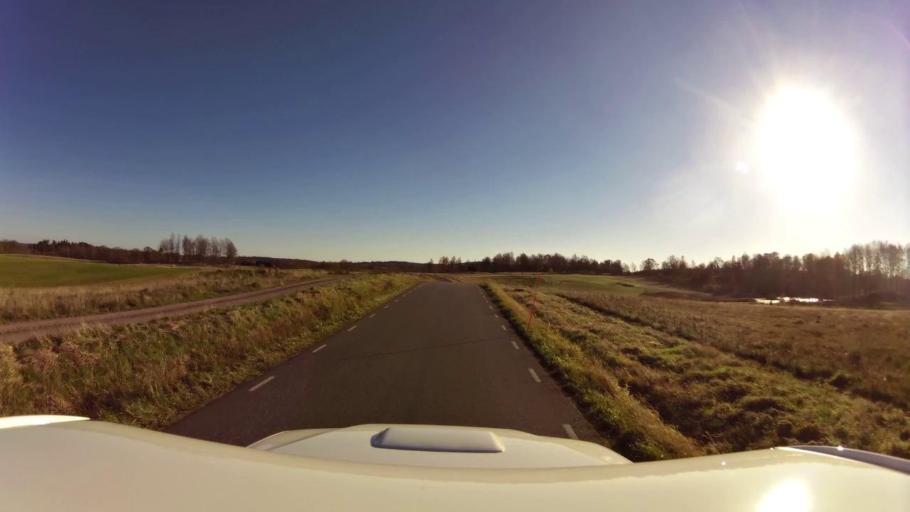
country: SE
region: OEstergoetland
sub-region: Kinda Kommun
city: Rimforsa
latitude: 58.2408
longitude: 15.6729
